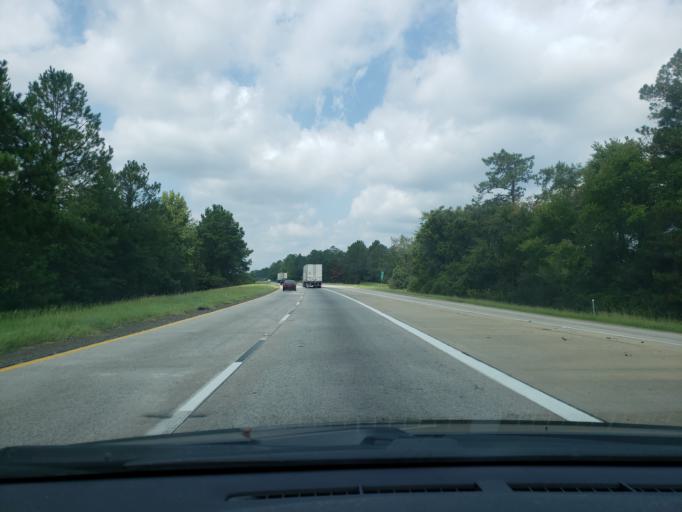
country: US
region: Georgia
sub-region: Treutlen County
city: Soperton
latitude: 32.4354
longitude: -82.5036
